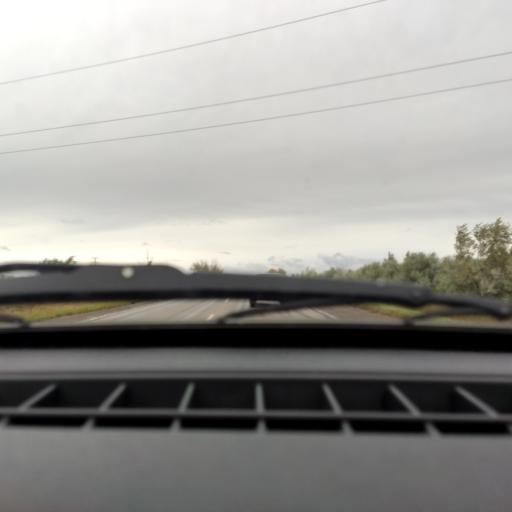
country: RU
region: Bashkortostan
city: Davlekanovo
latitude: 54.1804
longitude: 54.9677
